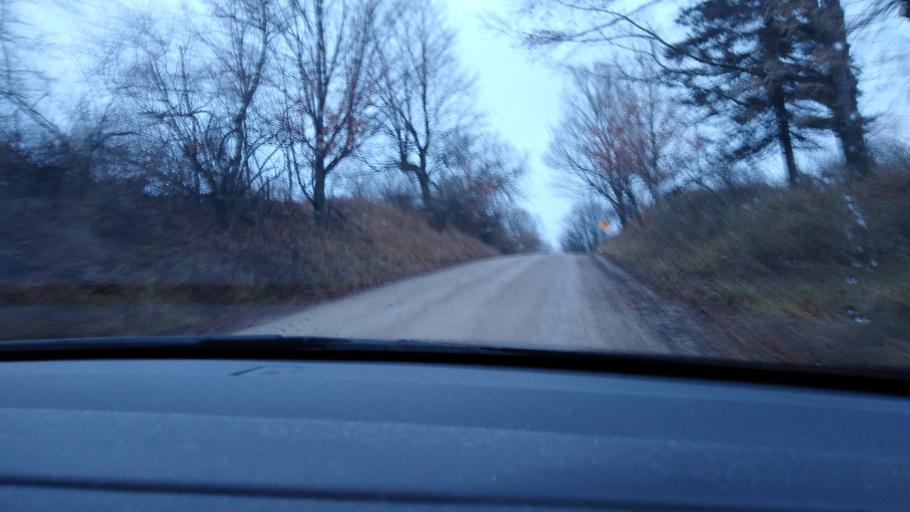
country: US
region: Michigan
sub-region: Wexford County
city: Cadillac
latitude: 44.1680
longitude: -85.3953
